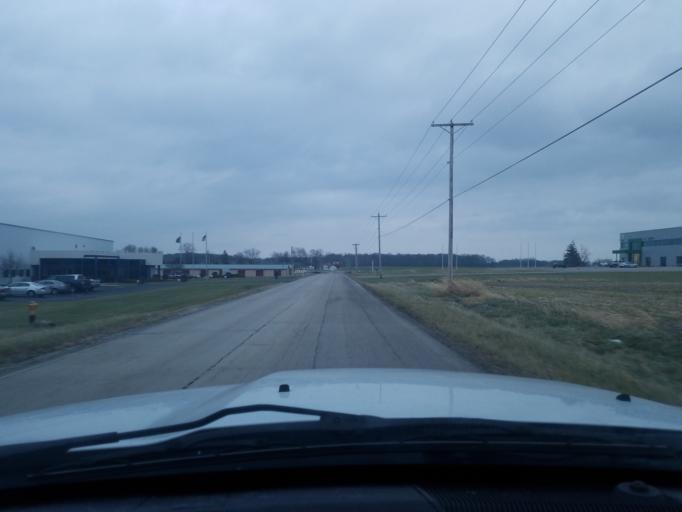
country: US
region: Indiana
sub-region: Wells County
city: Ossian
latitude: 40.8662
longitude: -85.1714
